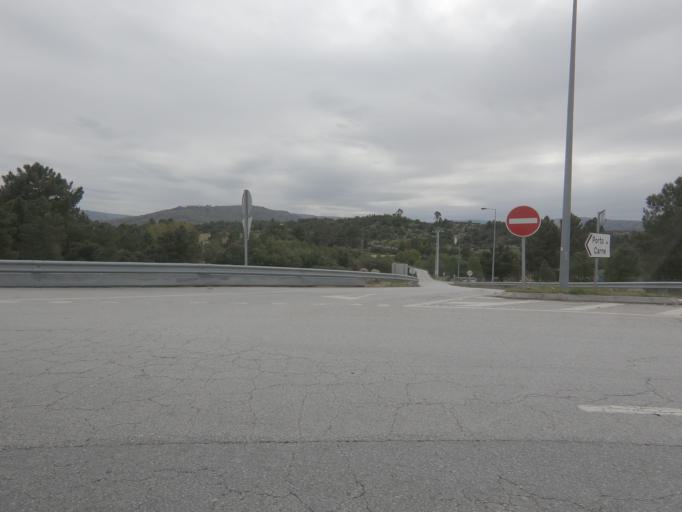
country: PT
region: Guarda
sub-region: Celorico da Beira
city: Celorico da Beira
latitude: 40.6394
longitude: -7.3257
